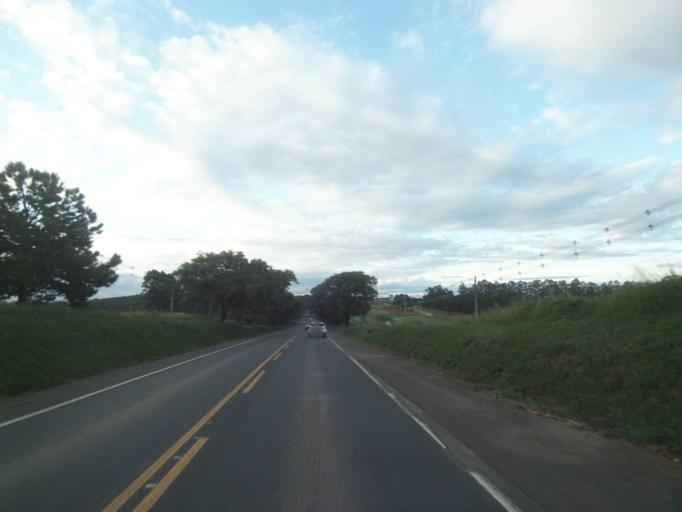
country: BR
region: Parana
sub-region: Telemaco Borba
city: Telemaco Borba
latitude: -24.3540
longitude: -50.6592
